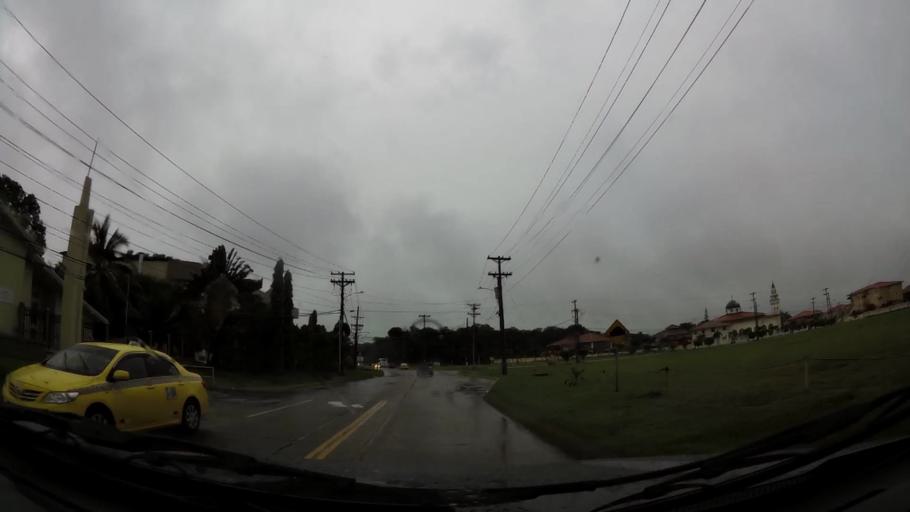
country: PA
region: Colon
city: Las Margaritas
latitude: 9.3247
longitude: -79.8946
